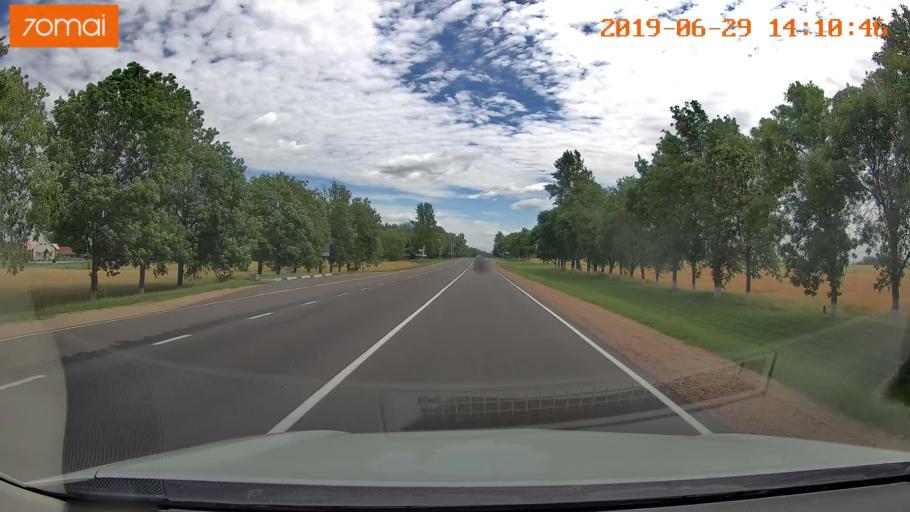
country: BY
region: Minsk
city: Salihorsk
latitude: 52.8253
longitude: 27.4982
